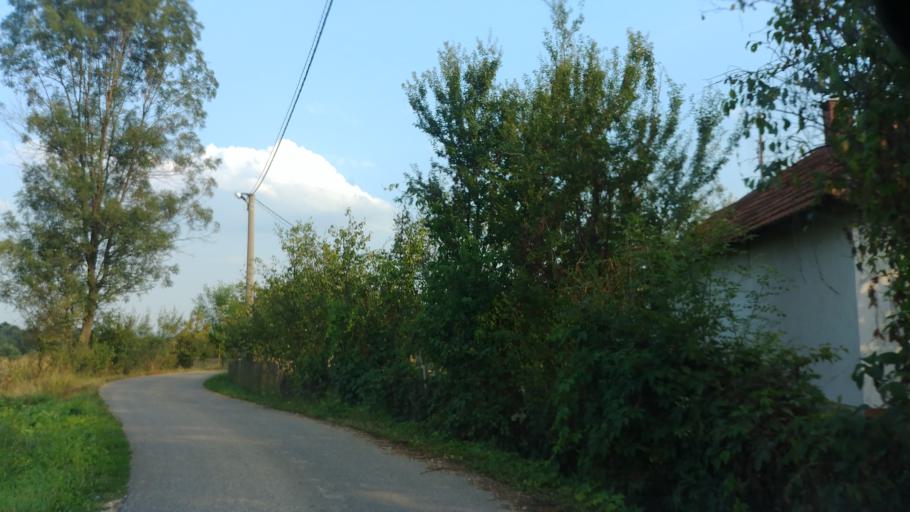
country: BA
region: Republika Srpska
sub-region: Opstina Ugljevik
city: Ugljevik
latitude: 44.7035
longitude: 19.0092
